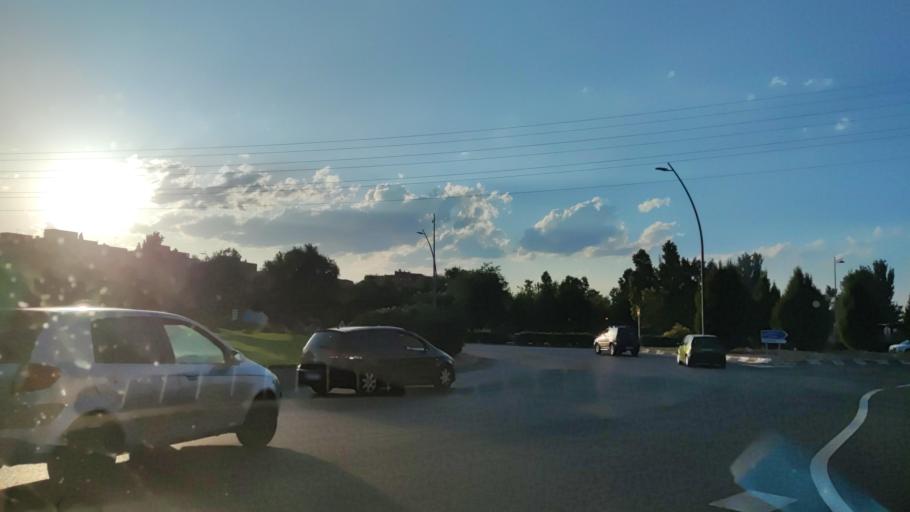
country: ES
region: Madrid
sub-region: Provincia de Madrid
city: Leganes
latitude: 40.3344
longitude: -3.7358
